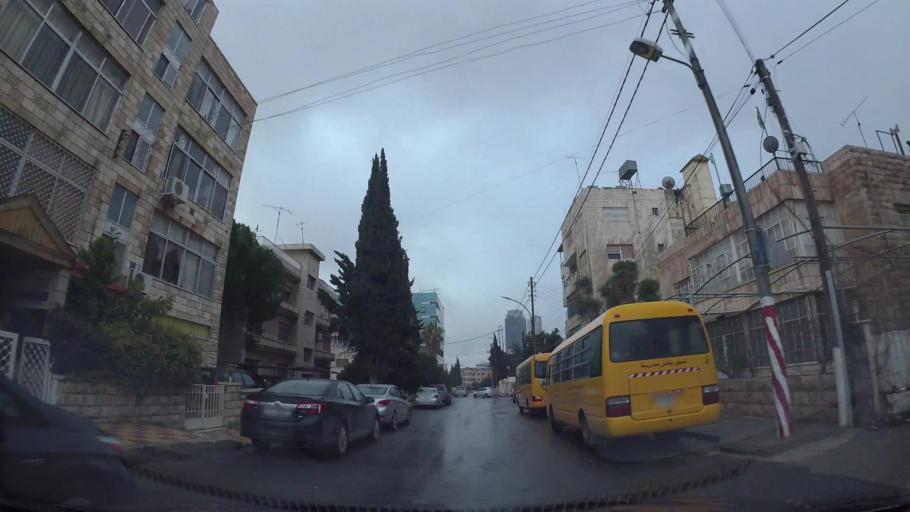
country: JO
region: Amman
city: Amman
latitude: 31.9703
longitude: 35.9116
